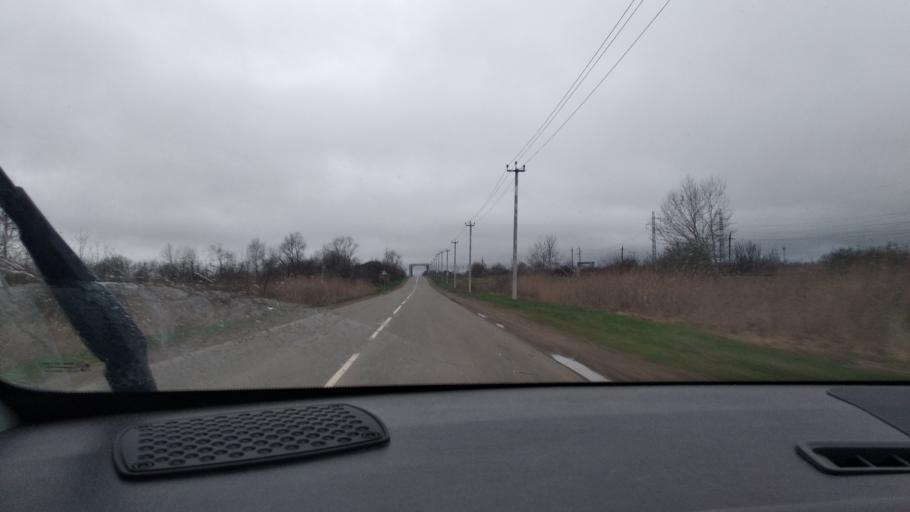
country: RU
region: Krasnodarskiy
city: Afipskiy
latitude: 44.8933
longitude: 38.8142
